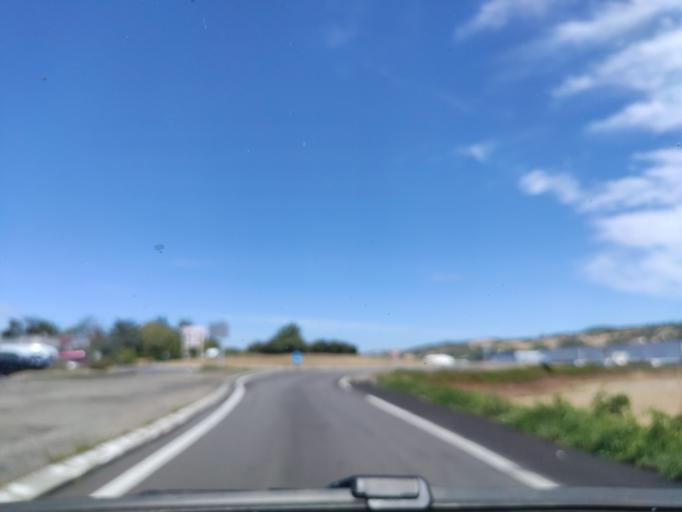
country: FR
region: Rhone-Alpes
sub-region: Departement de l'Isere
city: Reventin-Vaugris
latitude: 45.4585
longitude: 4.8254
